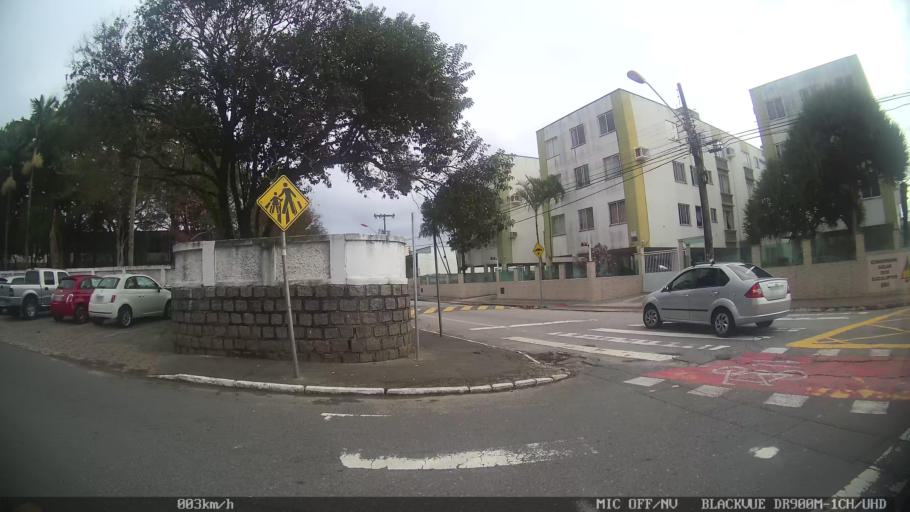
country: BR
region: Santa Catarina
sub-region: Sao Jose
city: Campinas
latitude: -27.5545
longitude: -48.6236
